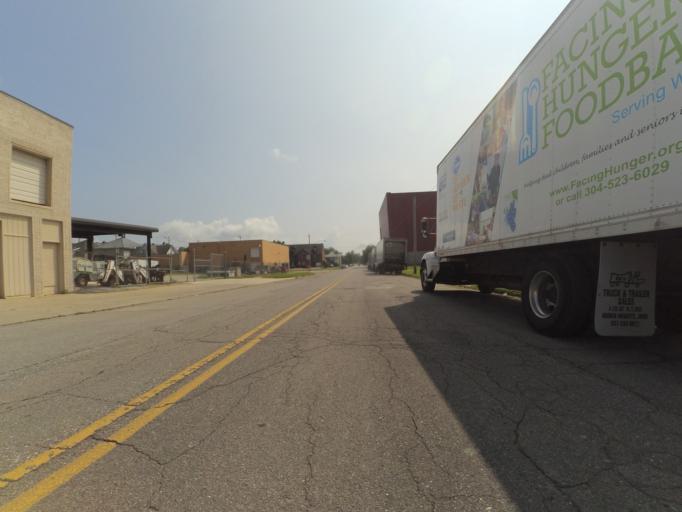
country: US
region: West Virginia
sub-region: Cabell County
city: Huntington
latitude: 38.4177
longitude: -82.4368
